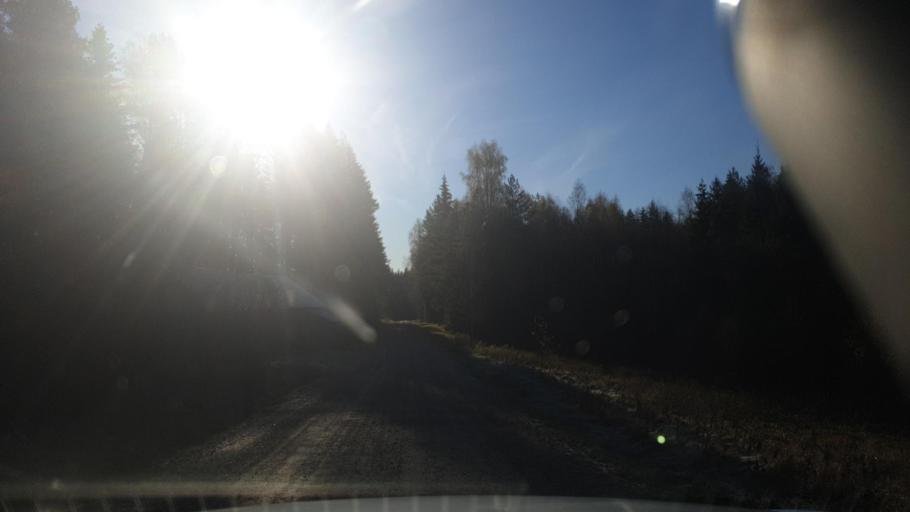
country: SE
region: Vaermland
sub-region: Karlstads Kommun
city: Edsvalla
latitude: 59.5342
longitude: 12.9946
